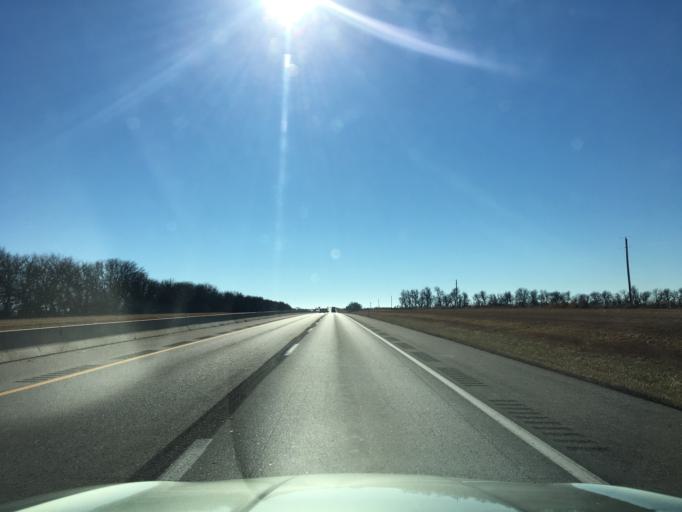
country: US
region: Kansas
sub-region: Sumner County
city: Wellington
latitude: 37.0826
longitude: -97.3386
